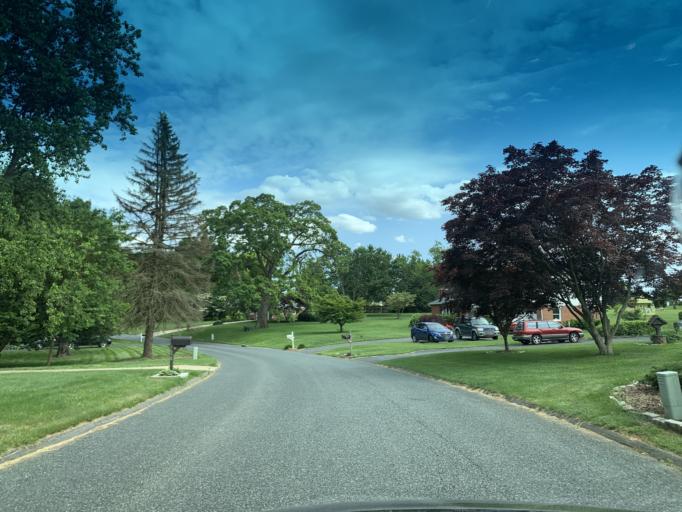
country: US
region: Maryland
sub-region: Harford County
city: Jarrettsville
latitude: 39.6048
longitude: -76.4683
